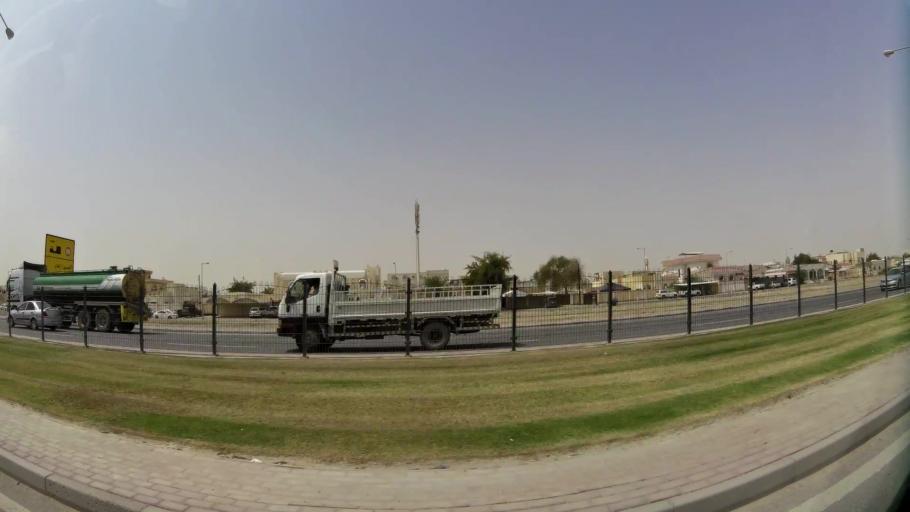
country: QA
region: Baladiyat ar Rayyan
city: Ar Rayyan
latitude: 25.2446
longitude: 51.4313
